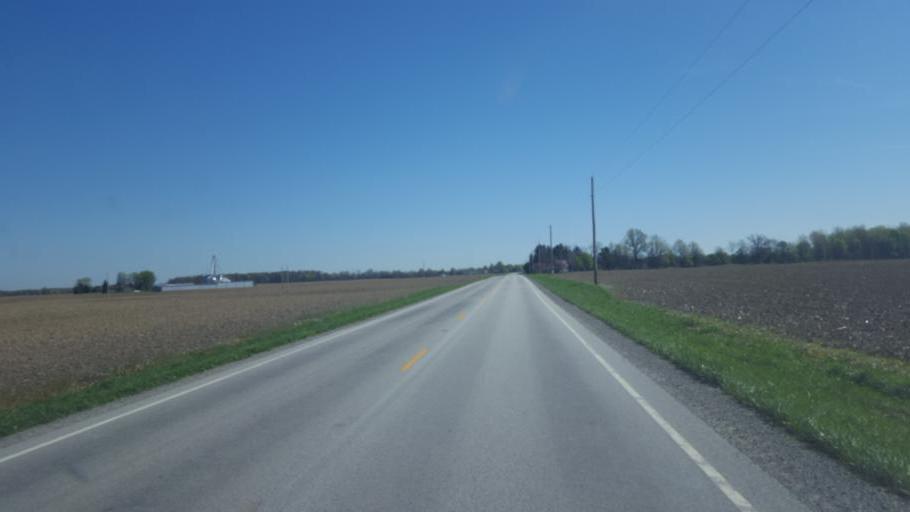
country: US
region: Ohio
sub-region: Wyandot County
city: Upper Sandusky
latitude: 40.9398
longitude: -83.1880
